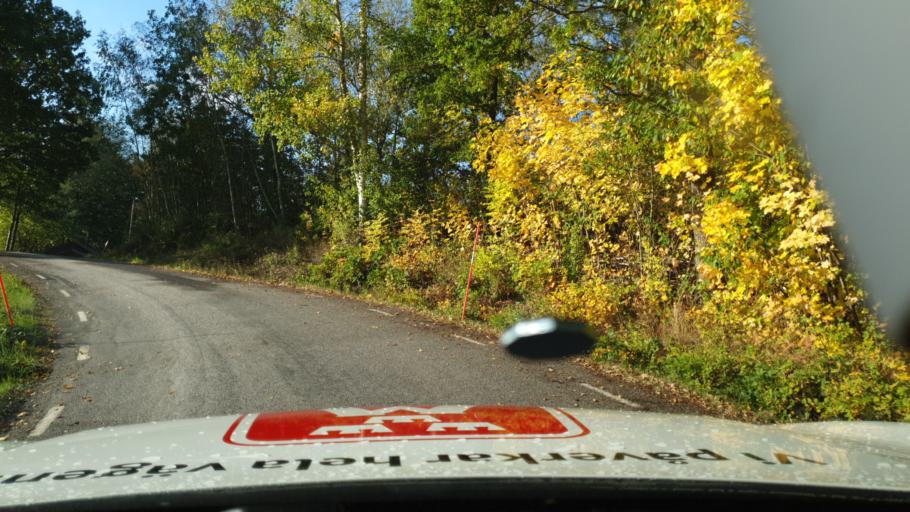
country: SE
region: Kalmar
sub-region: Vasterviks Kommun
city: Forserum
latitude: 57.9993
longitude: 16.5113
